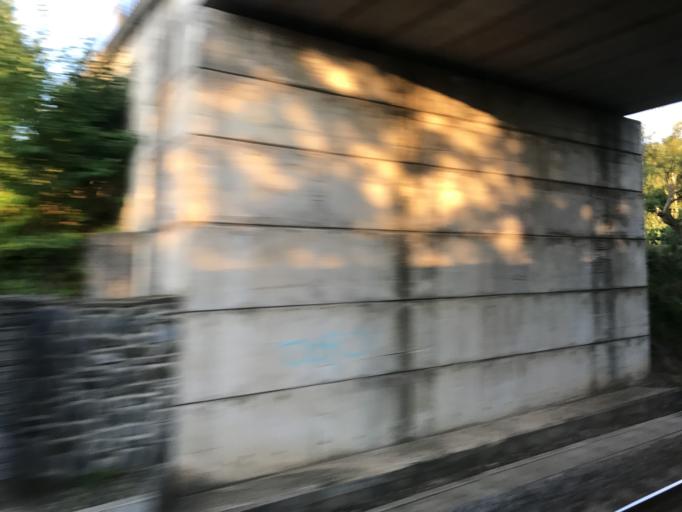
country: CZ
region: Central Bohemia
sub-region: Okres Benesov
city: Benesov
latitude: 49.7672
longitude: 14.6901
